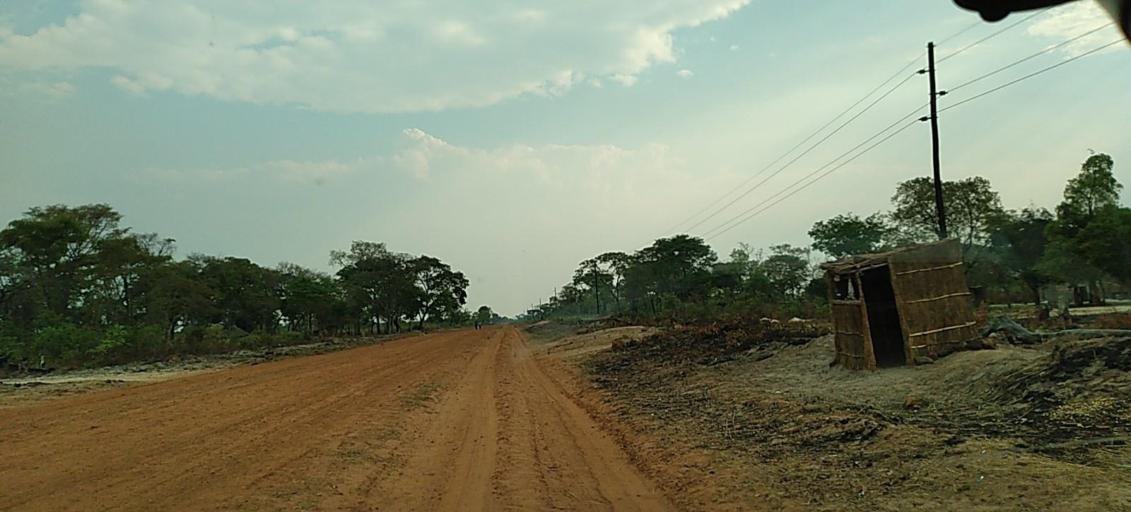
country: ZM
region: North-Western
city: Kabompo
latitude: -13.8860
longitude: 23.6617
